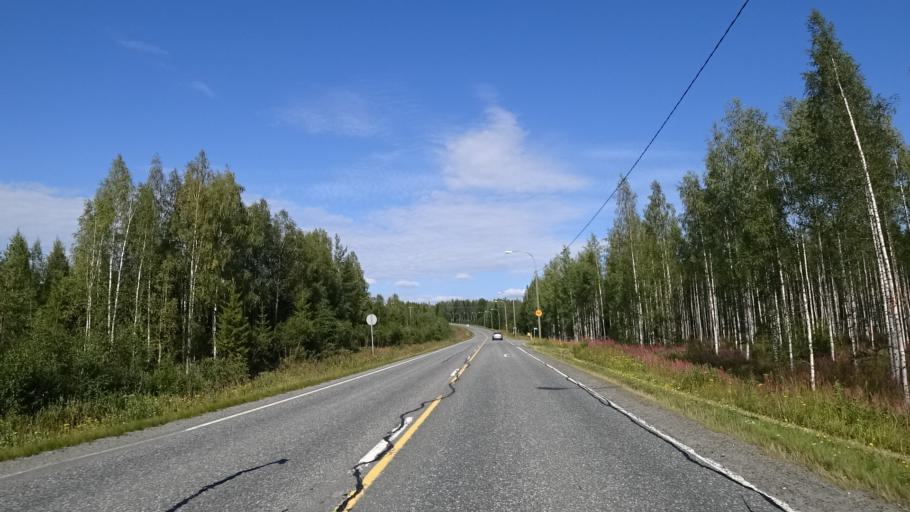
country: FI
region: North Karelia
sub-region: Joensuu
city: Eno
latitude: 62.7781
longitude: 30.0658
